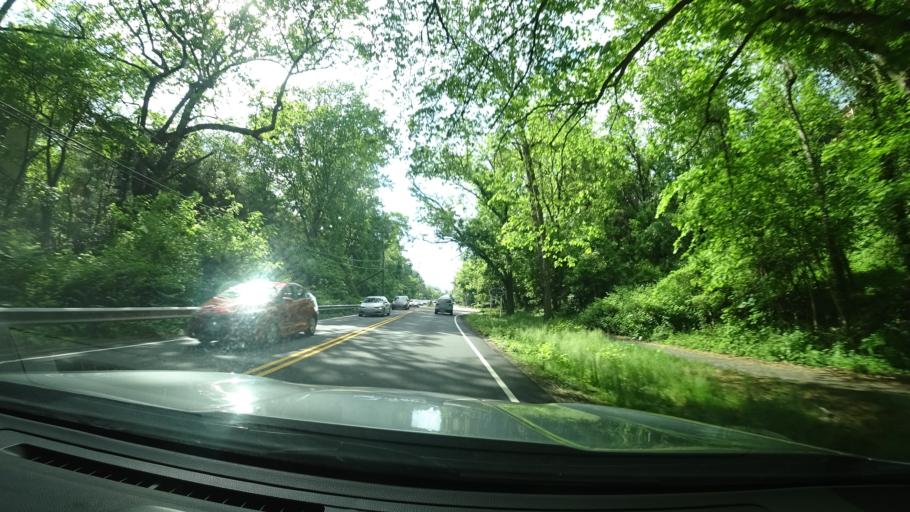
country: US
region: Virginia
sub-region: Fairfax County
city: McLean
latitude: 38.9301
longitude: -77.1704
